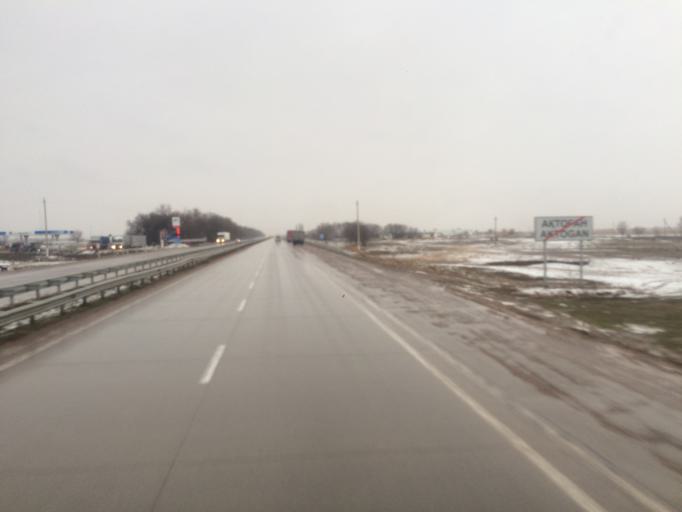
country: KZ
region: Zhambyl
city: Merke
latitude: 42.8780
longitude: 73.0986
